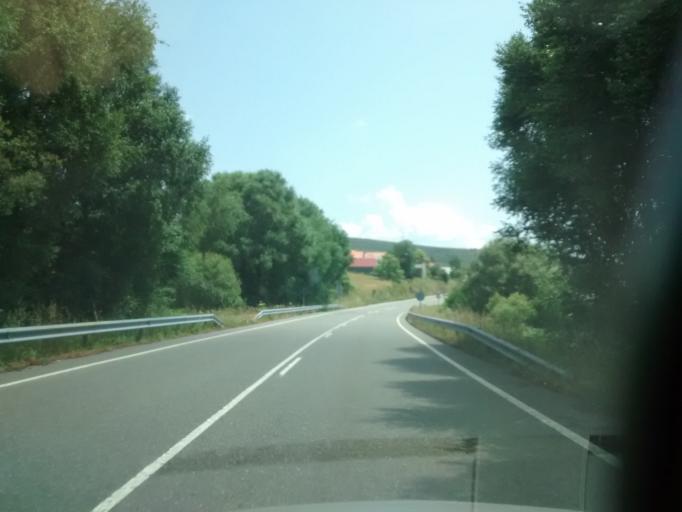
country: ES
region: Galicia
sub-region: Provincia de Ourense
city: Avion
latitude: 42.5044
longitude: -8.2535
